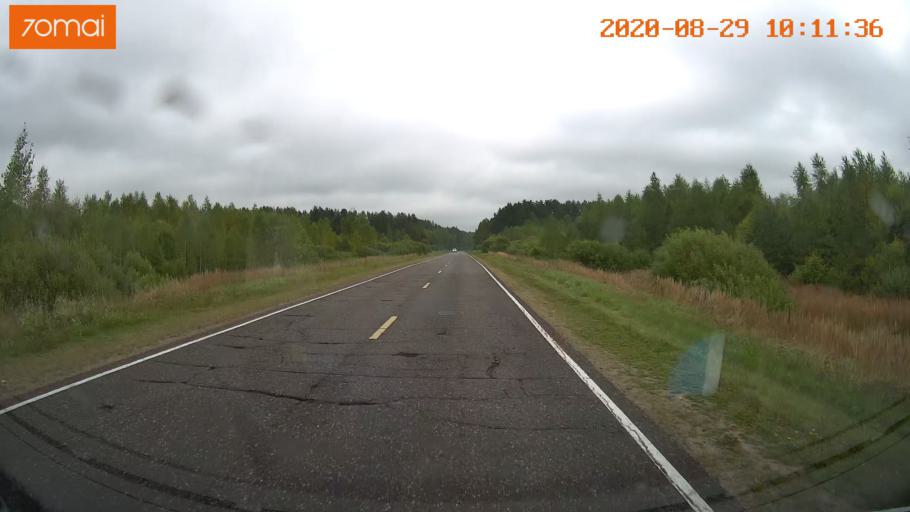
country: RU
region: Ivanovo
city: Kuznechikha
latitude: 57.3754
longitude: 42.6877
